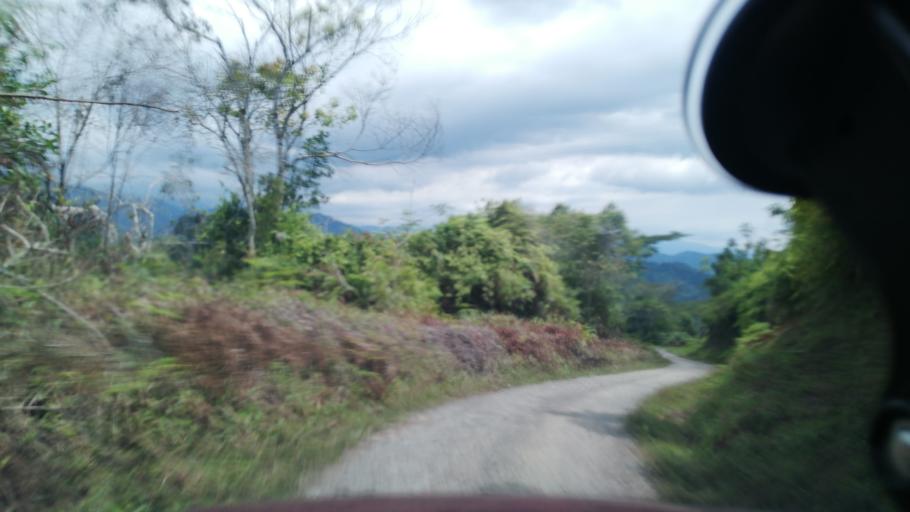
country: CO
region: Cundinamarca
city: Vergara
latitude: 5.1775
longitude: -74.2739
